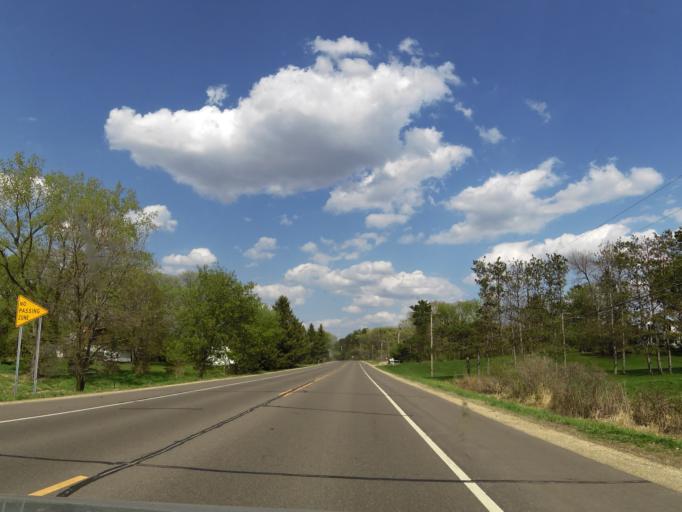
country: US
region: Minnesota
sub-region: Washington County
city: Oak Park Heights
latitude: 45.0097
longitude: -92.8155
